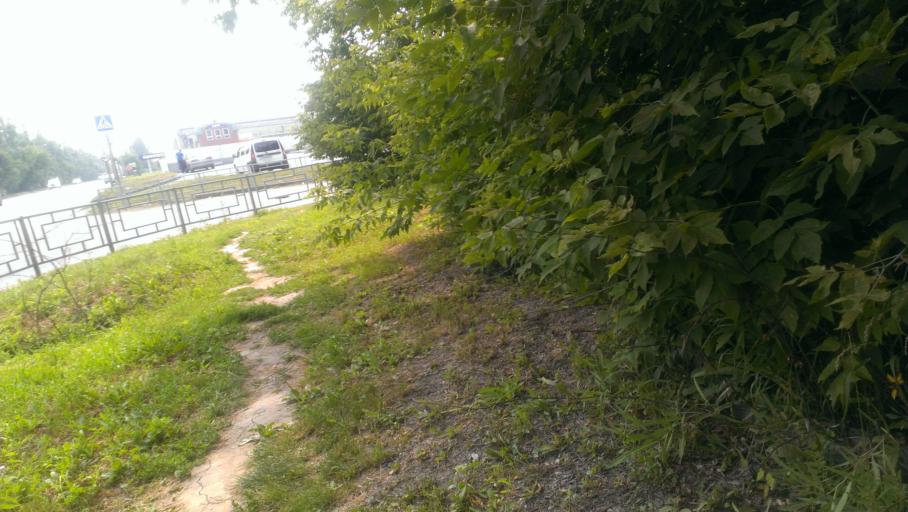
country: RU
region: Altai Krai
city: Novosilikatnyy
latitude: 53.3635
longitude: 83.6603
